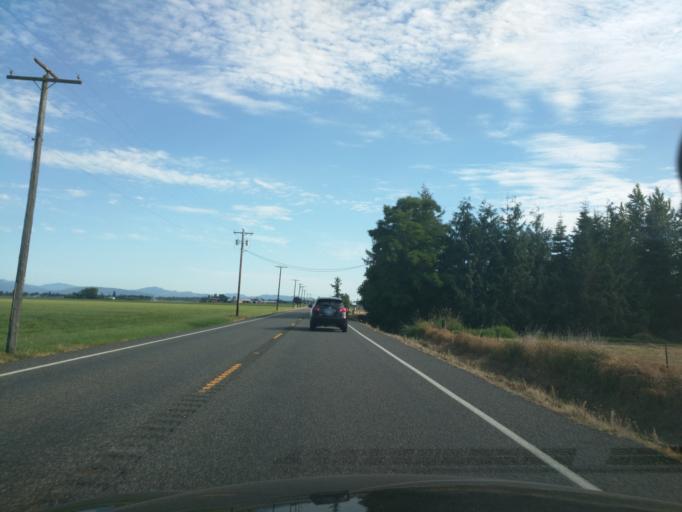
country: US
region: Washington
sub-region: Whatcom County
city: Lynden
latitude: 48.9785
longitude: -122.4852
